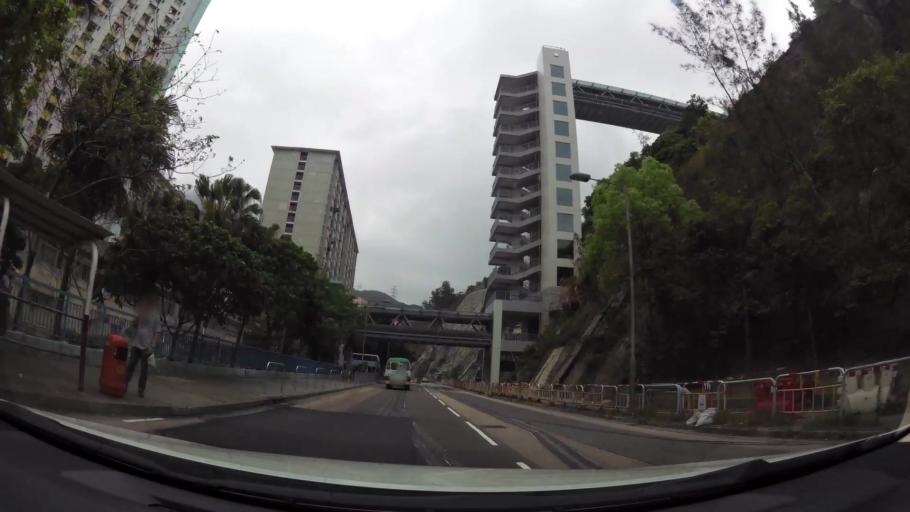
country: HK
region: Kowloon City
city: Kowloon
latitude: 22.3290
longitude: 114.2270
